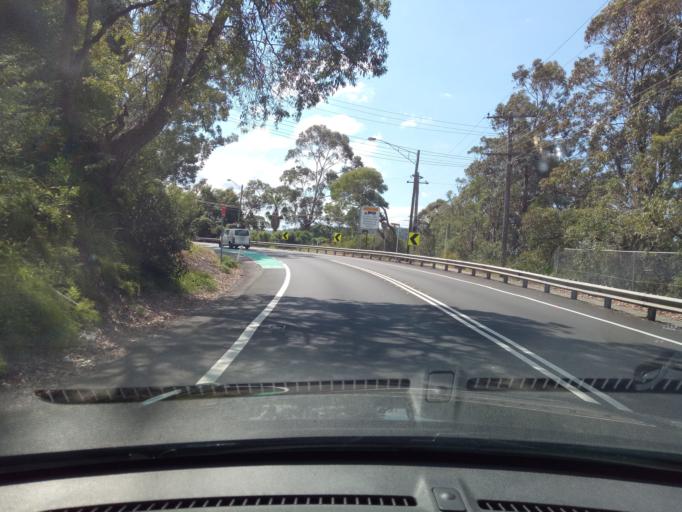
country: AU
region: New South Wales
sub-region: Gosford Shire
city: Point Clare
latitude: -33.4410
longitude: 151.3296
